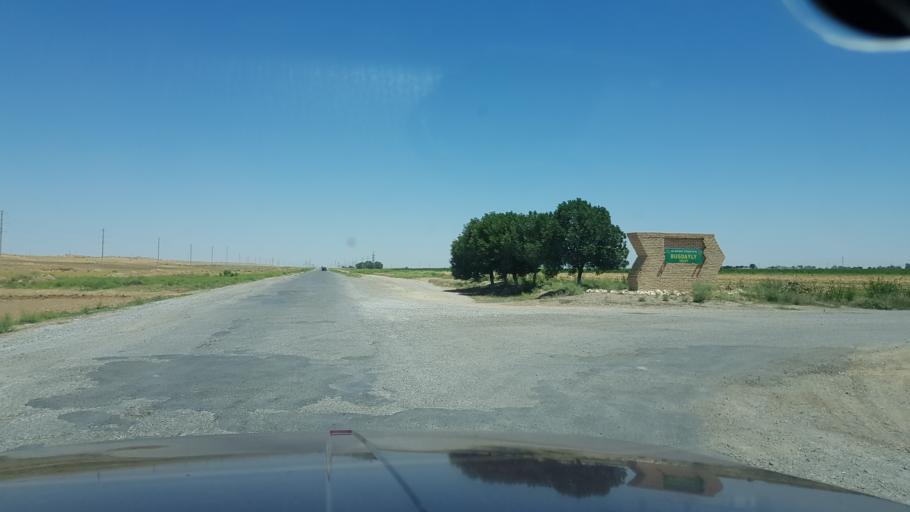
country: TM
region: Ahal
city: Annau
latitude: 37.8609
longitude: 58.7098
